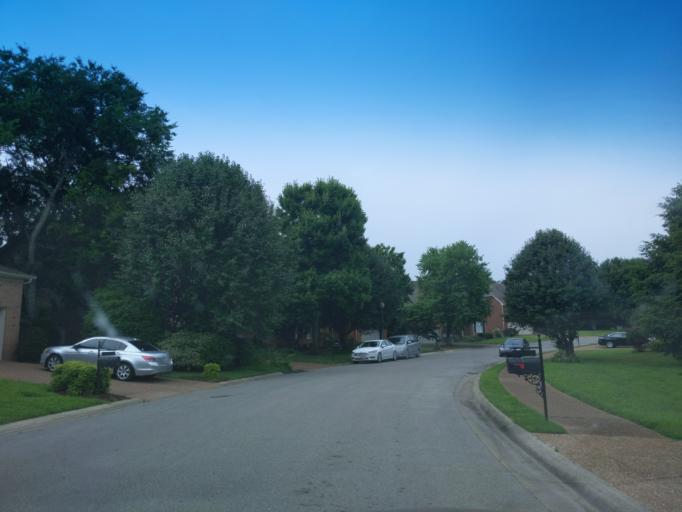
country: US
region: Tennessee
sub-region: Williamson County
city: Brentwood Estates
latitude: 36.0350
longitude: -86.7627
